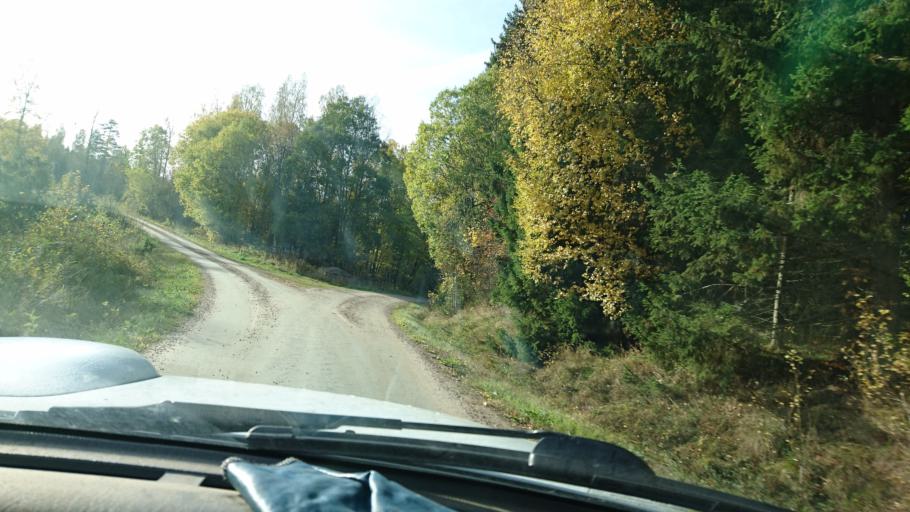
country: SE
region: Vaestra Goetaland
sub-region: Ulricehamns Kommun
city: Ulricehamn
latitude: 57.9541
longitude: 13.5265
